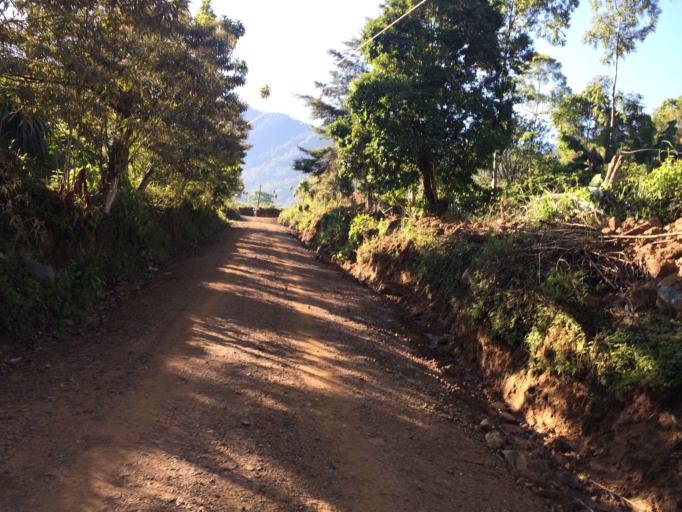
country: CR
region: San Jose
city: San Isidro
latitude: 9.4553
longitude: -83.5971
